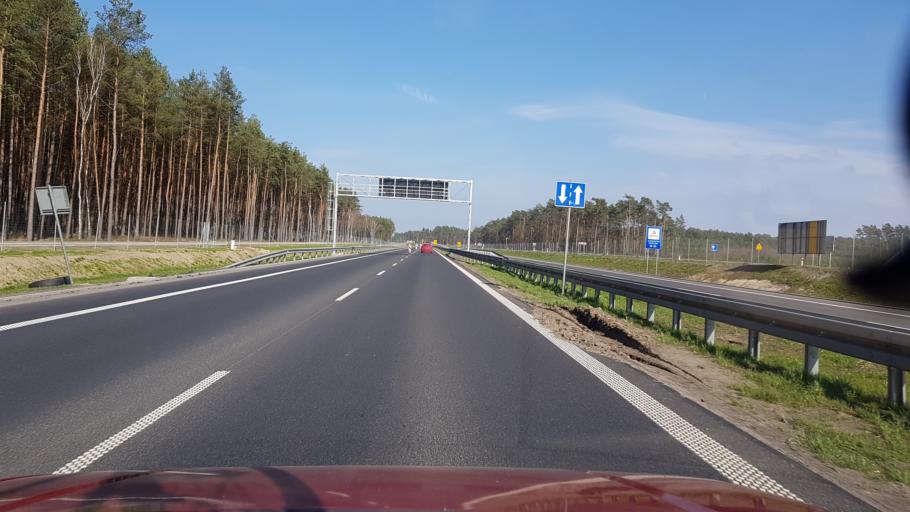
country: PL
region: West Pomeranian Voivodeship
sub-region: Powiat goleniowski
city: Goleniow
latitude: 53.5994
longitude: 14.8832
